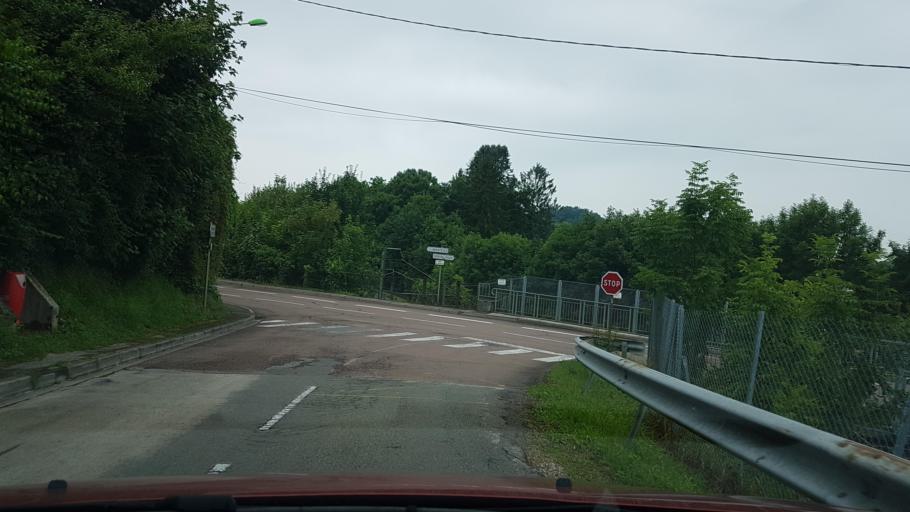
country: FR
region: Franche-Comte
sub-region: Departement du Jura
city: Lons-le-Saunier
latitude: 46.6714
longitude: 5.5388
